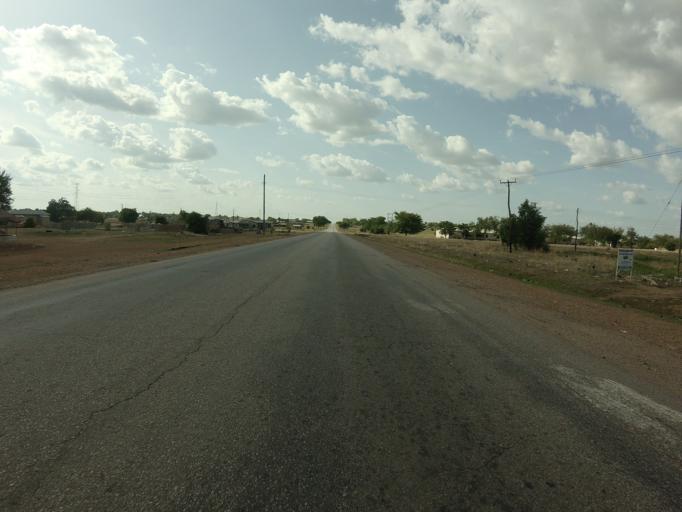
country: GH
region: Upper East
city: Bolgatanga
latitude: 10.6813
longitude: -0.8622
